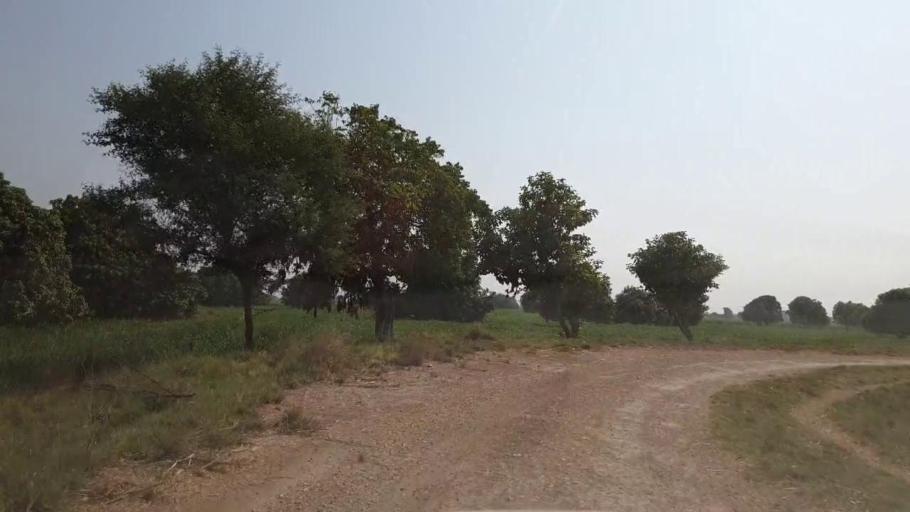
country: PK
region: Sindh
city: Mirpur Khas
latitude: 25.6445
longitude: 69.1532
